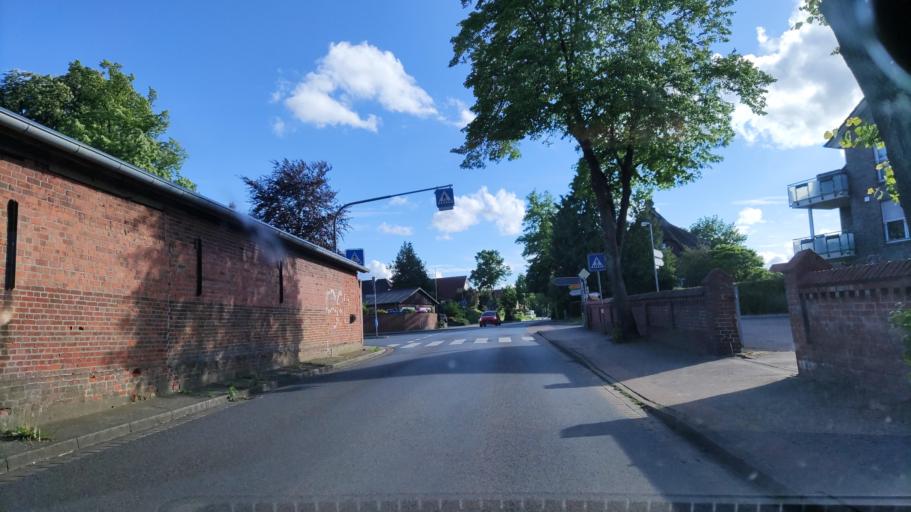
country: DE
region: Lower Saxony
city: Stelle
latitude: 53.3799
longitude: 10.1109
